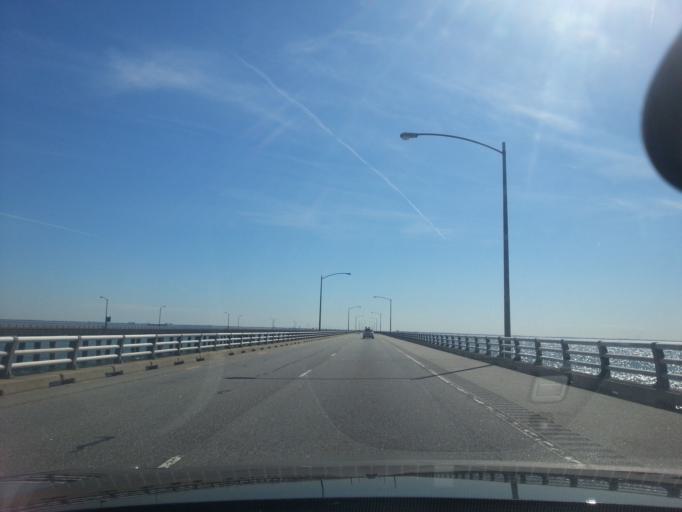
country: US
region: Virginia
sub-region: City of Virginia Beach
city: Virginia Beach
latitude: 37.0216
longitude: -76.0907
